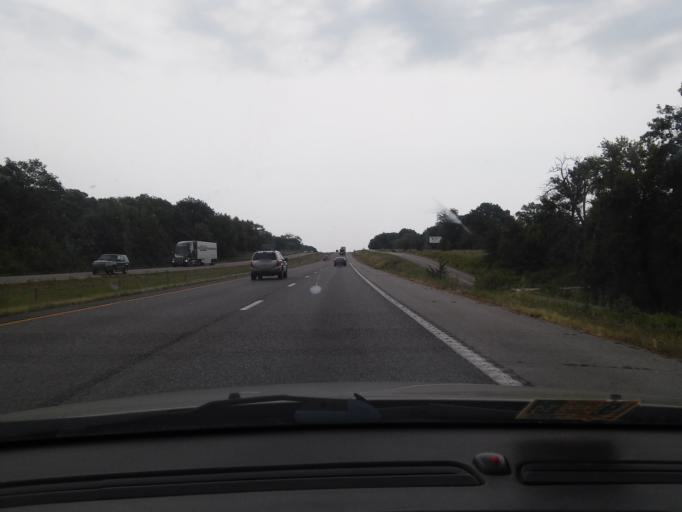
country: US
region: Missouri
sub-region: Boone County
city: Columbia
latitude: 38.9581
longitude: -92.1734
